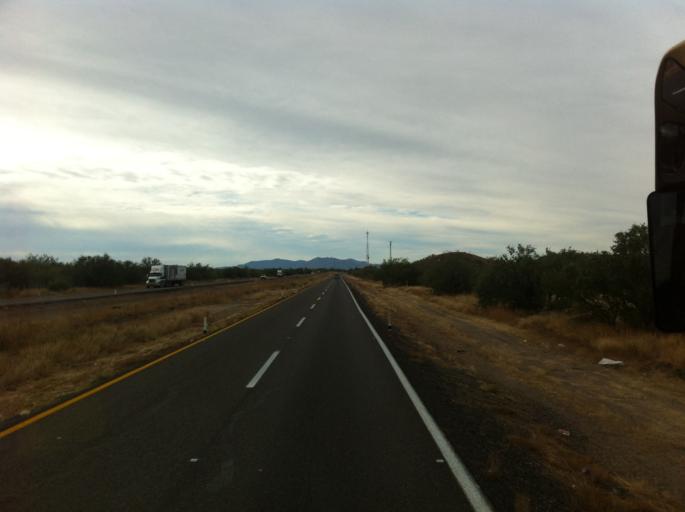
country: MX
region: Sonora
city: Hermosillo
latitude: 28.8117
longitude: -110.9583
